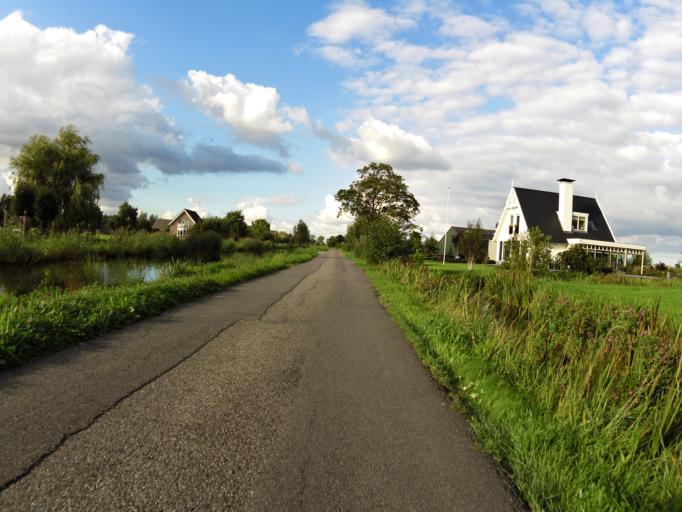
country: NL
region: Utrecht
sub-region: Gemeente Woerden
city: Woerden
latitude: 52.1303
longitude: 4.8938
